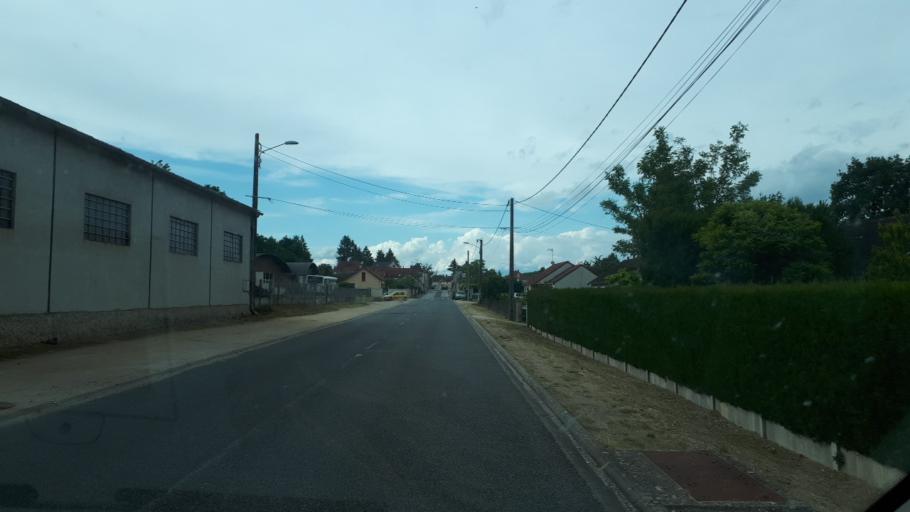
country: FR
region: Centre
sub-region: Departement du Loir-et-Cher
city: Villefranche-sur-Cher
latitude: 47.2795
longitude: 1.7750
